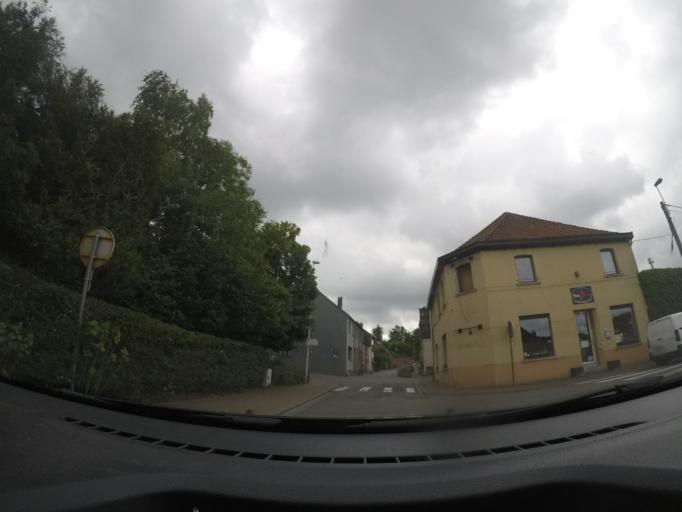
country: BE
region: Flanders
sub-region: Provincie Vlaams-Brabant
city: Sint-Genesius-Rode
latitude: 50.7473
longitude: 4.3540
